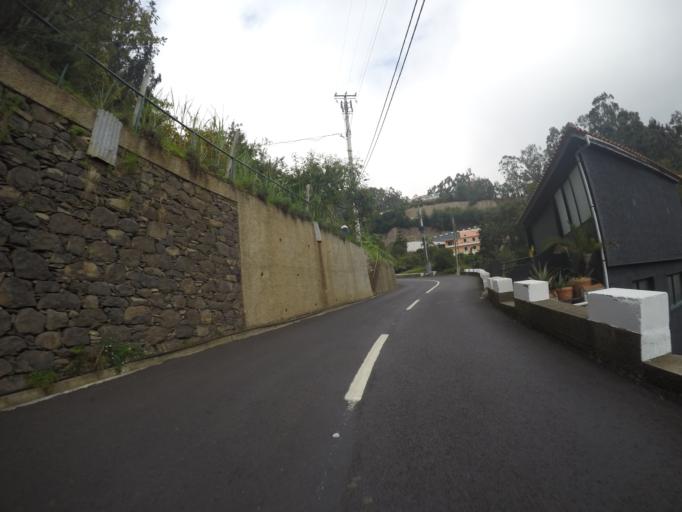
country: PT
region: Madeira
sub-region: Camara de Lobos
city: Curral das Freiras
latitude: 32.6876
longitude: -16.9531
